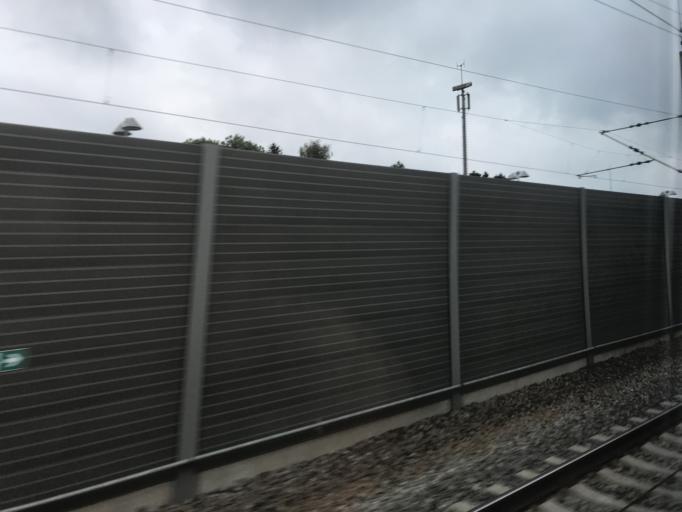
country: DE
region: Bavaria
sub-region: Upper Bavaria
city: Hattenhofen
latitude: 48.2226
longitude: 11.1004
